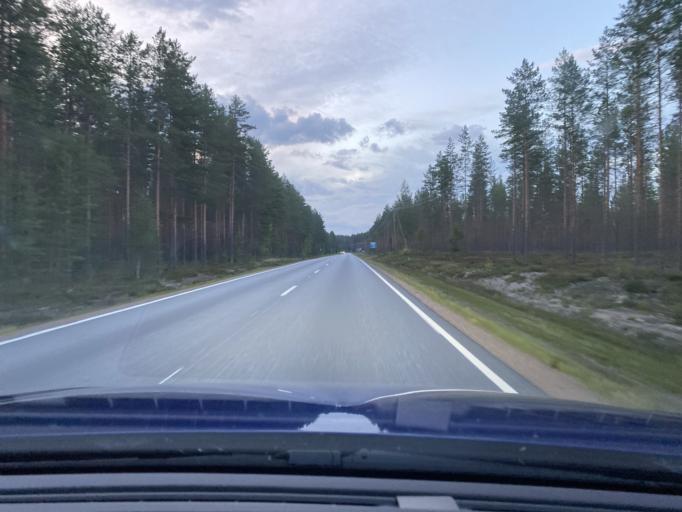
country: FI
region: Satakunta
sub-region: Pohjois-Satakunta
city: Honkajoki
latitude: 62.2056
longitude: 22.2997
